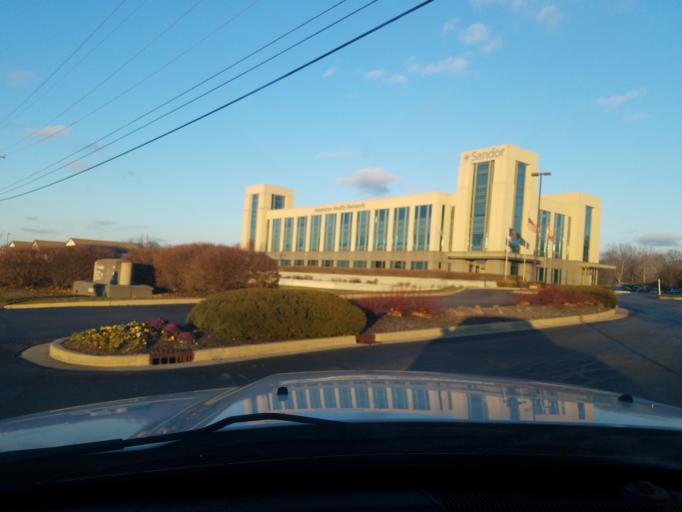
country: US
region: Indiana
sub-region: Hamilton County
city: Carmel
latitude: 39.9460
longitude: -86.1554
